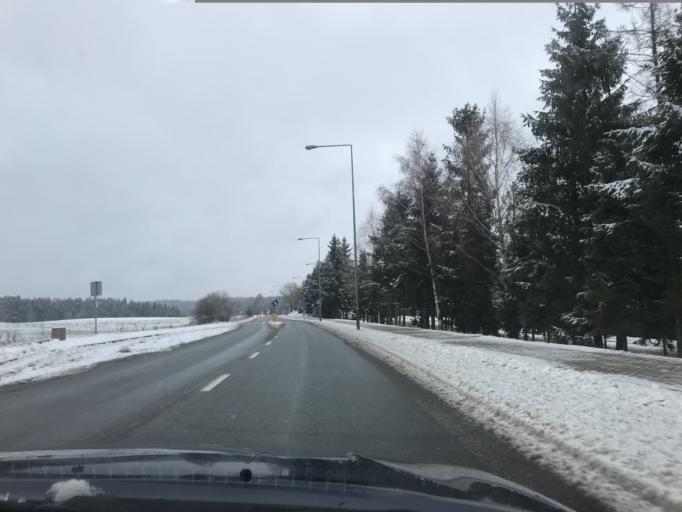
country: PL
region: Pomeranian Voivodeship
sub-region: Powiat bytowski
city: Bytow
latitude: 54.1890
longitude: 17.5101
